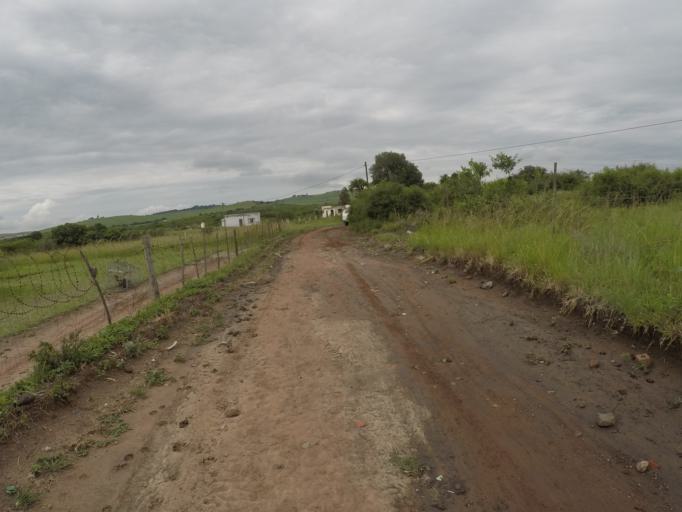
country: ZA
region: KwaZulu-Natal
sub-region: uThungulu District Municipality
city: Empangeni
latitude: -28.7155
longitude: 31.8614
